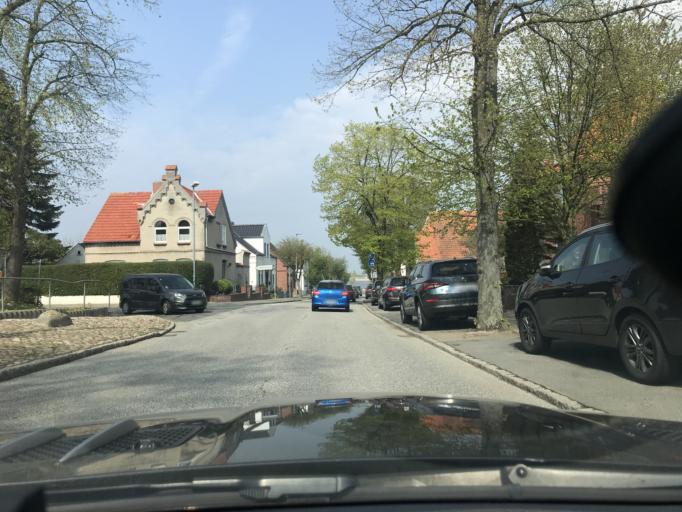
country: DE
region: Schleswig-Holstein
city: Heiligenhafen
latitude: 54.3727
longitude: 10.9743
